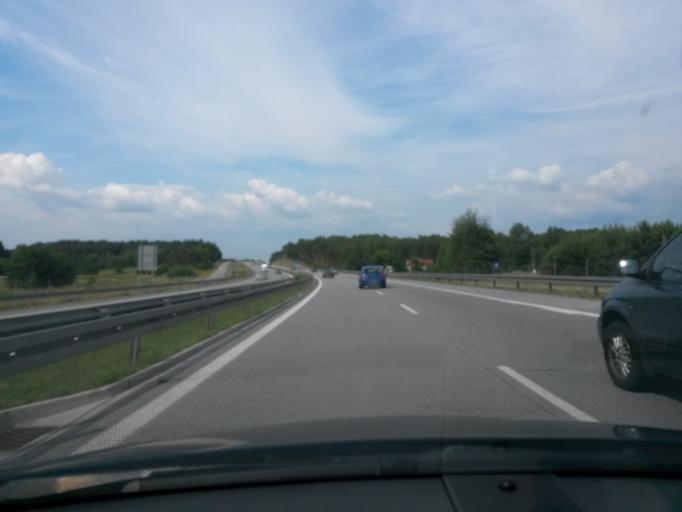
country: PL
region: Lodz Voivodeship
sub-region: Powiat tomaszowski
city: Czerniewice
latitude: 51.6954
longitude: 20.2144
